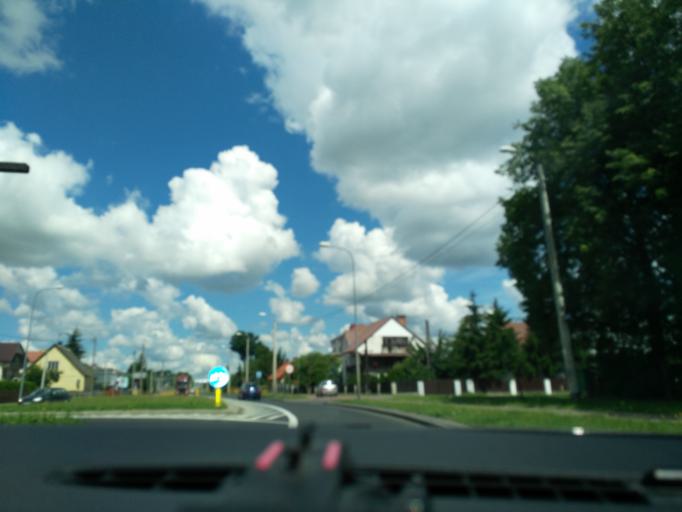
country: PL
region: Podlasie
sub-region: Powiat bielski
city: Bielsk Podlaski
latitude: 52.7785
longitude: 23.1884
